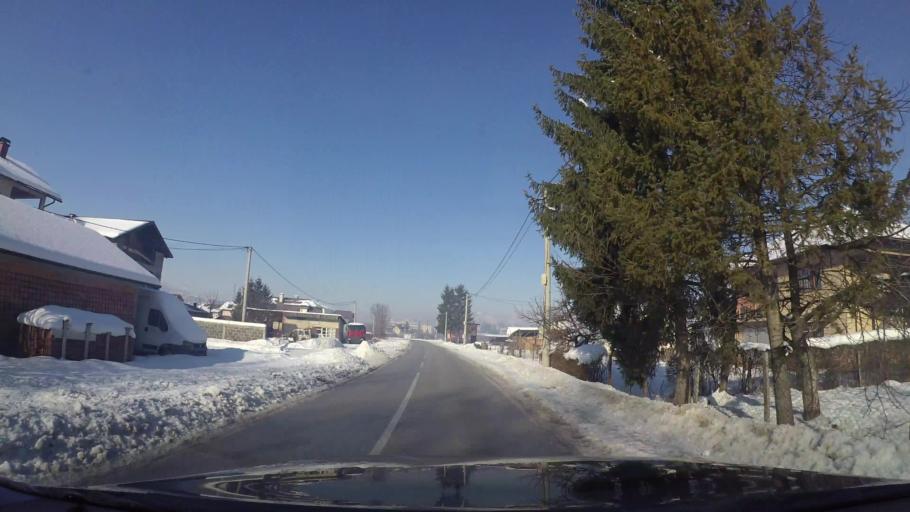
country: BA
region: Federation of Bosnia and Herzegovina
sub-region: Kanton Sarajevo
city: Sarajevo
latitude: 43.8204
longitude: 18.3810
